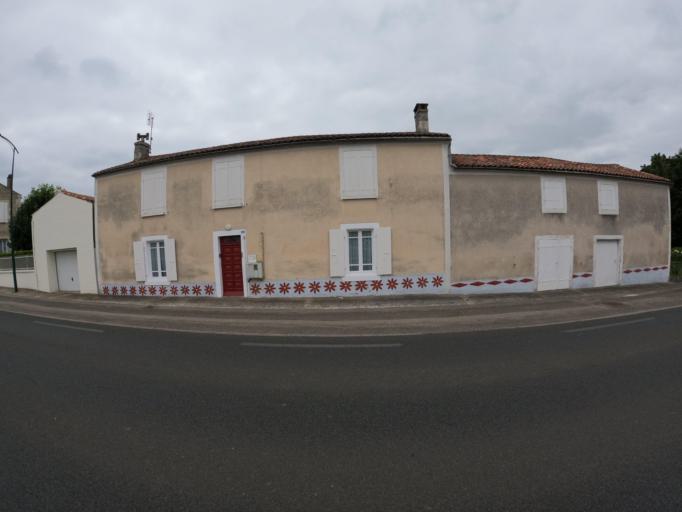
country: FR
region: Pays de la Loire
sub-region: Departement de la Vendee
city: Saint-Hilaire-des-Loges
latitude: 46.4025
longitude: -0.6706
